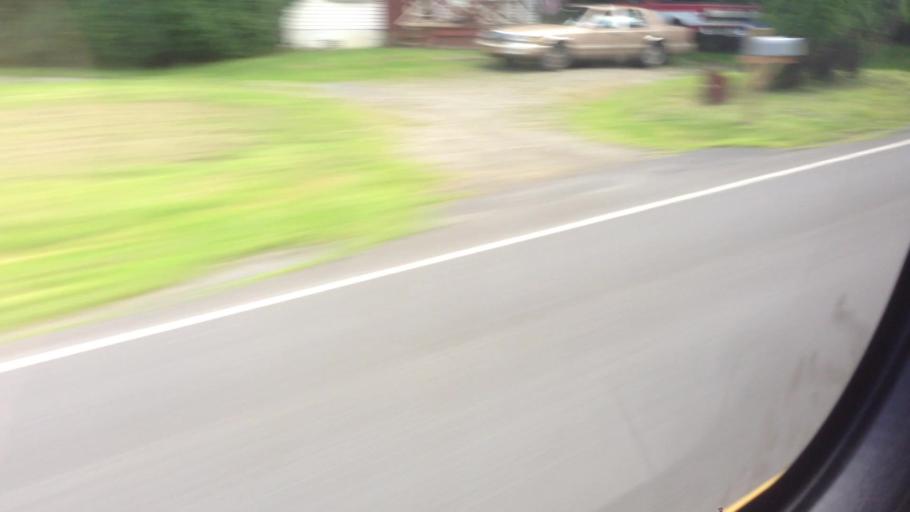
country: US
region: New York
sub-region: Dutchess County
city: Tivoli
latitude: 42.0425
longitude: -73.8951
